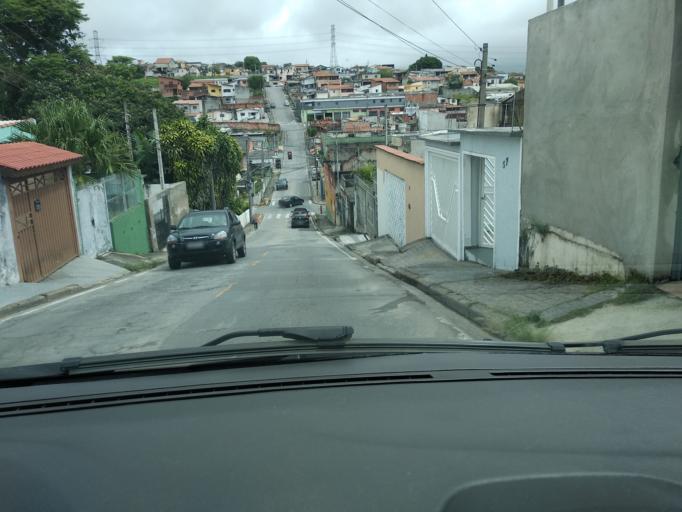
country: BR
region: Sao Paulo
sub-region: Mogi das Cruzes
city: Mogi das Cruzes
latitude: -23.5317
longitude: -46.1808
